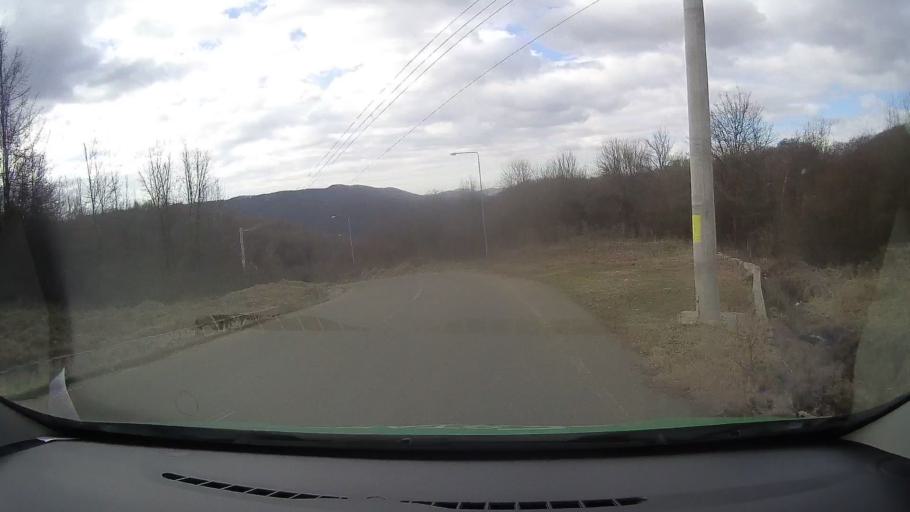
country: RO
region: Prahova
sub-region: Comuna Adunati
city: Adunati
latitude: 45.1319
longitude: 25.6140
